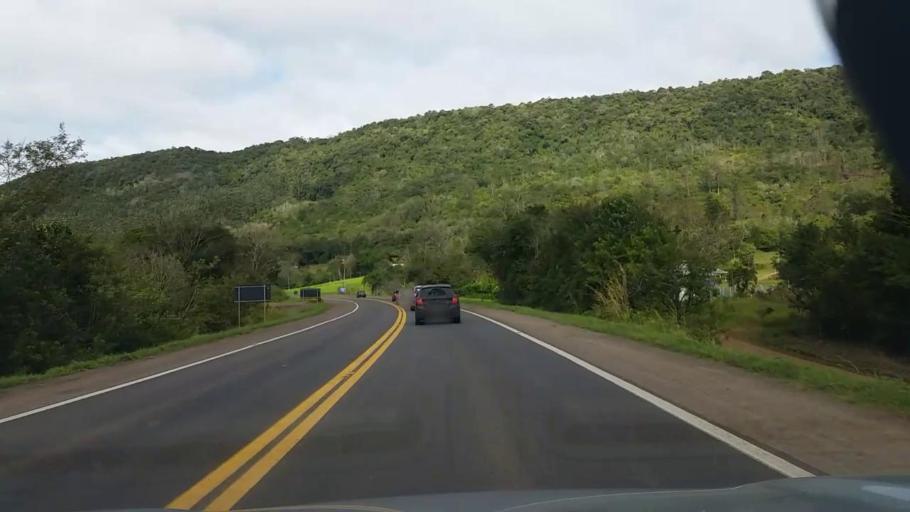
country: BR
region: Rio Grande do Sul
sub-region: Arroio Do Meio
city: Arroio do Meio
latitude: -29.3299
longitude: -52.1015
